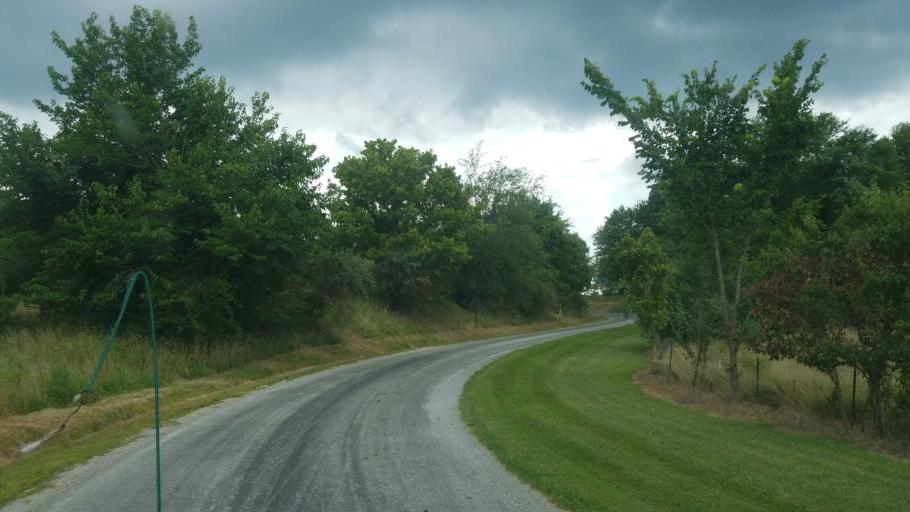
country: US
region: Illinois
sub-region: Jackson County
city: Murphysboro
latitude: 37.7172
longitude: -89.3265
